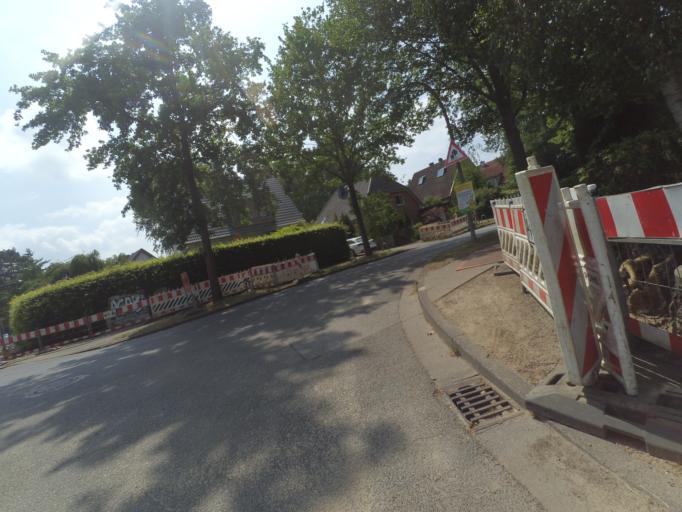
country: DE
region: Hamburg
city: Langenhorn
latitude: 53.6391
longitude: 9.9649
